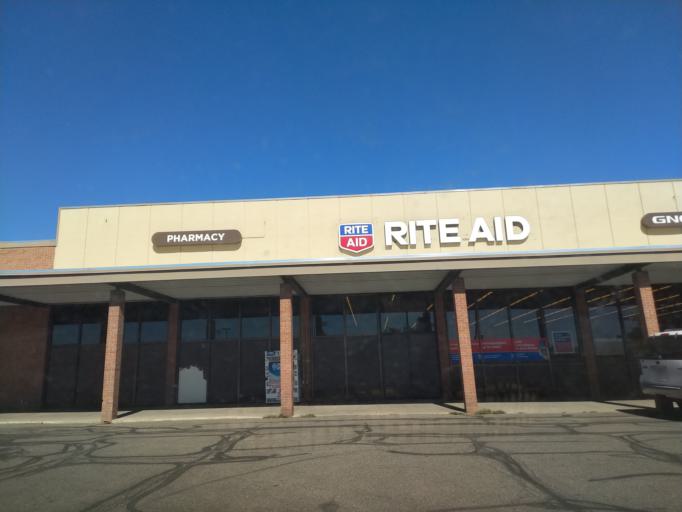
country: US
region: Colorado
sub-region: Mesa County
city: Grand Junction
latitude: 39.0837
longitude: -108.5514
